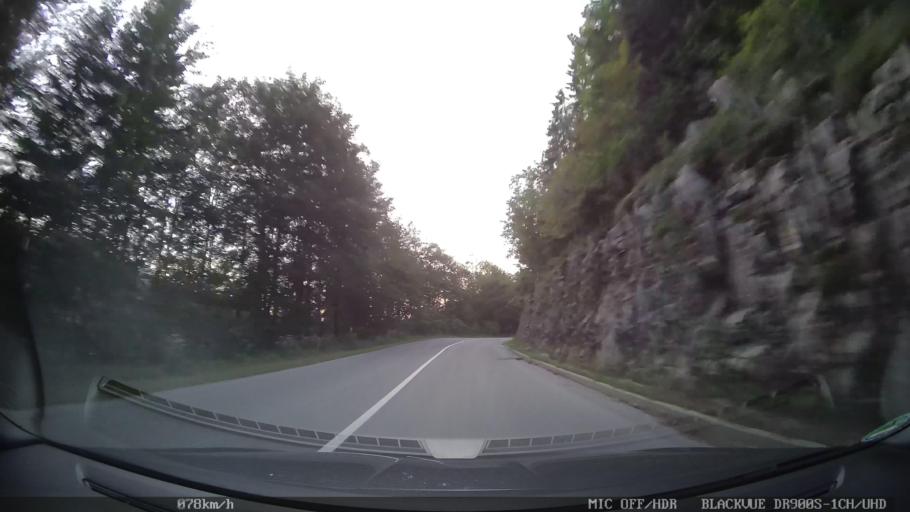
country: HR
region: Primorsko-Goranska
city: Novi Vinodolski
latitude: 45.1666
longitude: 14.9340
